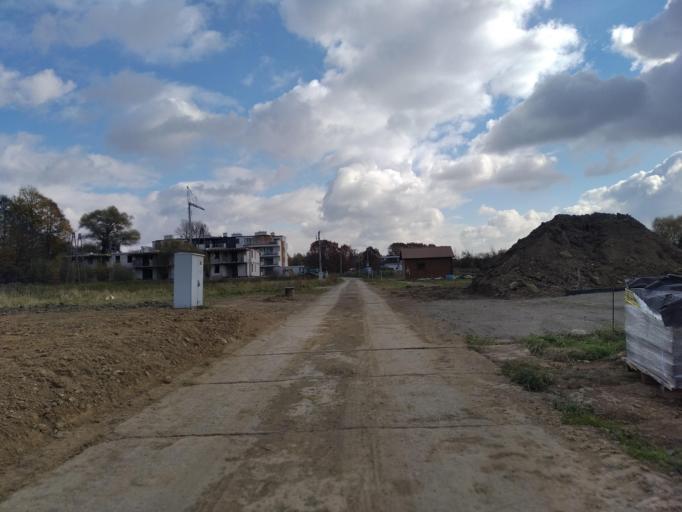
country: PL
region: Subcarpathian Voivodeship
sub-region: Powiat strzyzowski
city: Strzyzow
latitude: 49.8718
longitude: 21.7678
